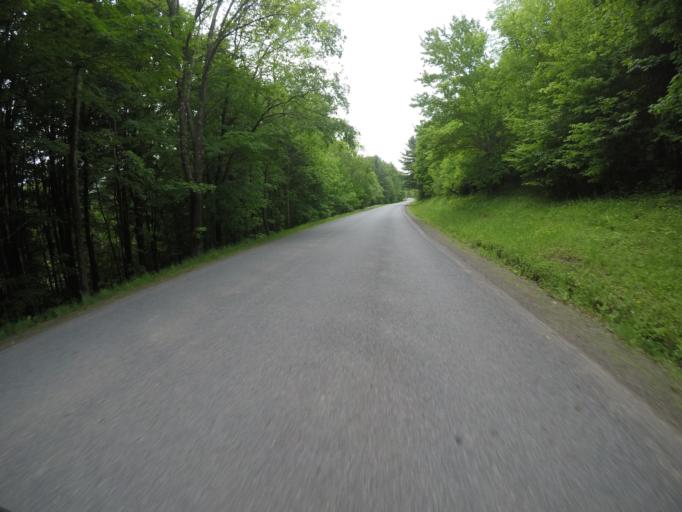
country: US
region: New York
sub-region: Delaware County
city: Stamford
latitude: 42.2182
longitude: -74.6830
